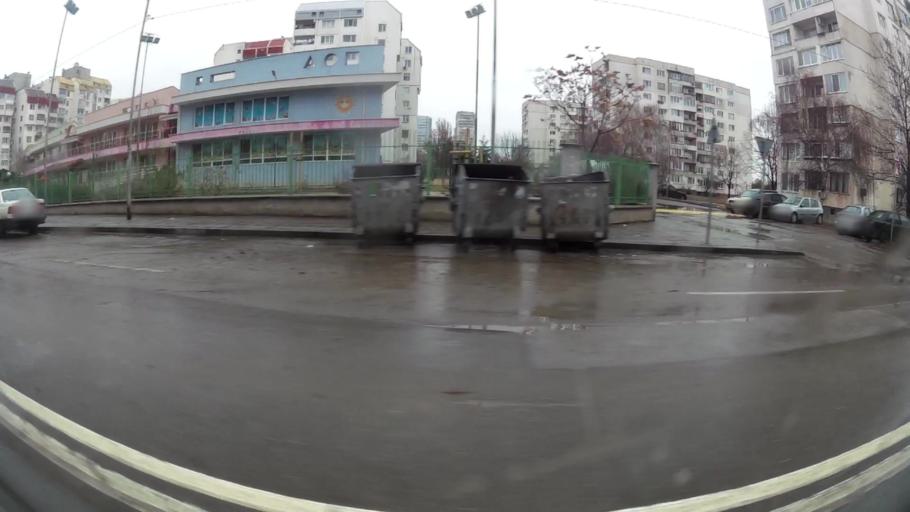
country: BG
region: Sofia-Capital
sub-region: Stolichna Obshtina
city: Sofia
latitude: 42.6412
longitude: 23.3855
